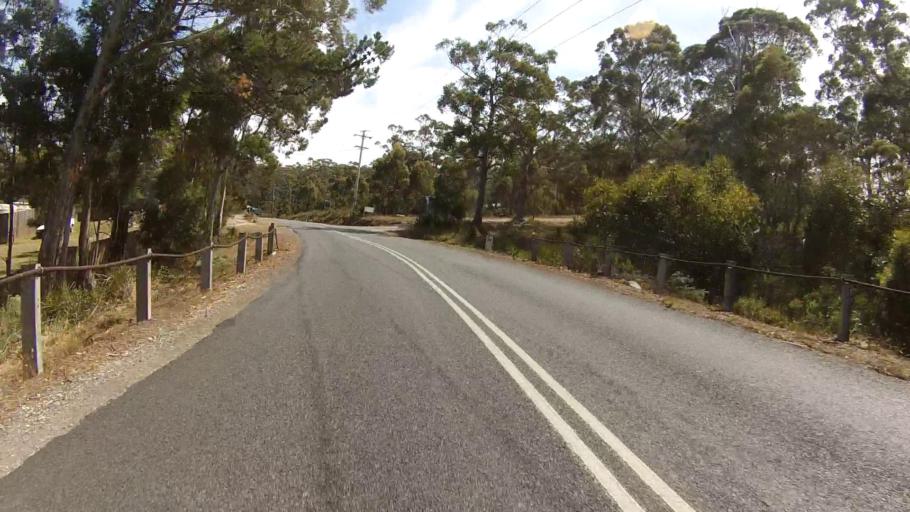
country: AU
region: Tasmania
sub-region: Huon Valley
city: Cygnet
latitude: -43.2699
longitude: 147.1476
